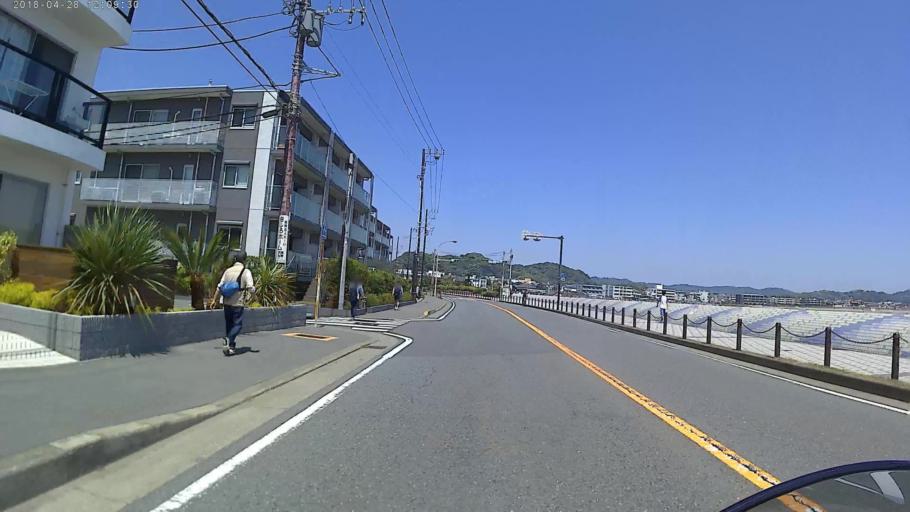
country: JP
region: Kanagawa
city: Kamakura
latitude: 35.3062
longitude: 139.5329
